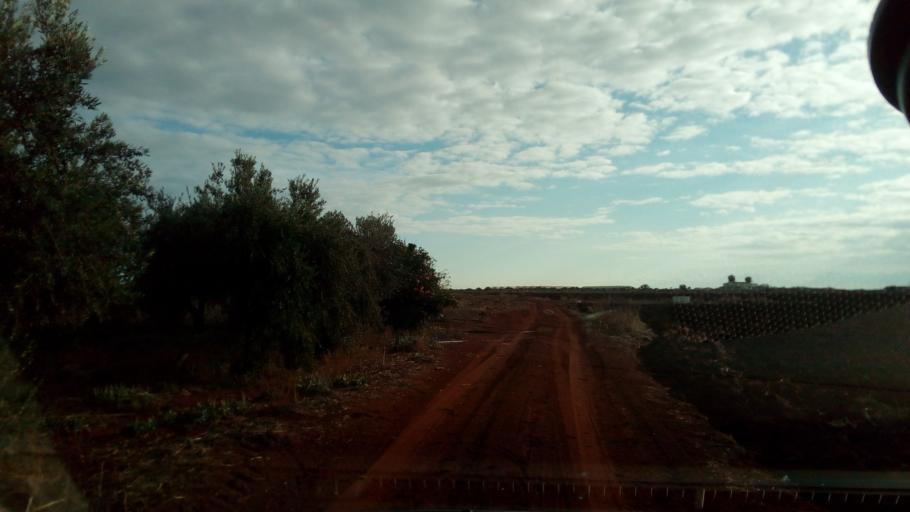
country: CY
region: Ammochostos
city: Avgorou
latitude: 35.0373
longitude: 33.8732
